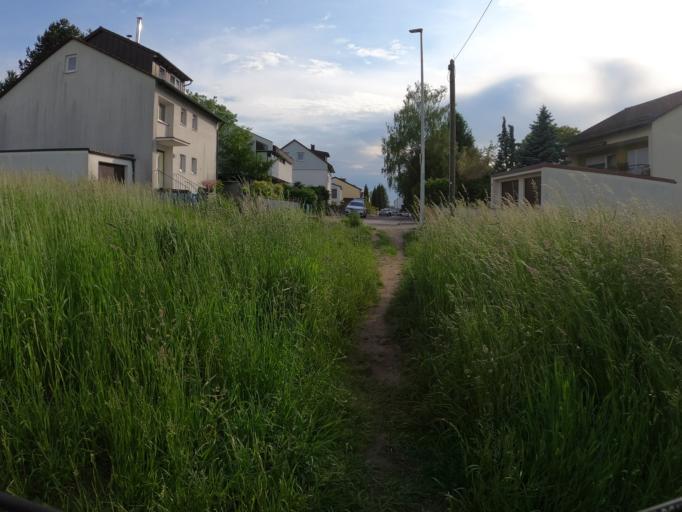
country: DE
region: Bavaria
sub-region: Swabia
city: Neu-Ulm
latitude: 48.4051
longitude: 10.0416
